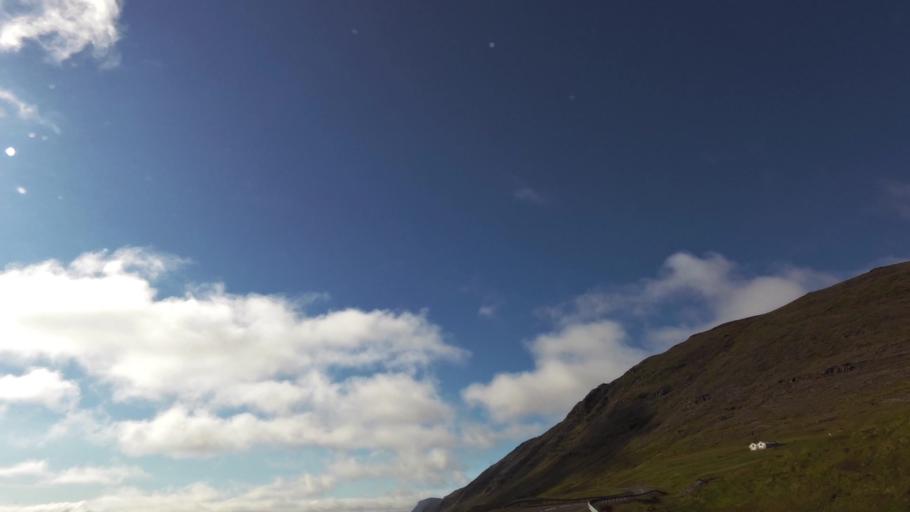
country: IS
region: West
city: Olafsvik
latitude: 65.5498
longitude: -23.8898
